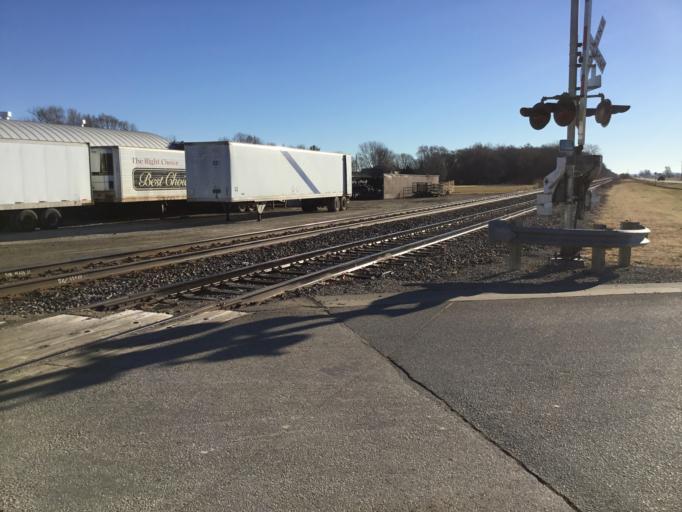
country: US
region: Kansas
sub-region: Shawnee County
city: Rossville
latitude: 39.1340
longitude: -95.9476
